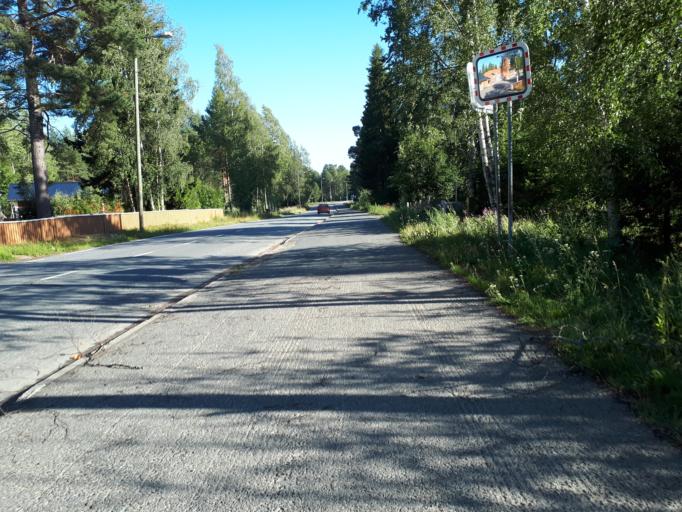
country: FI
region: Northern Ostrobothnia
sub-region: Oulunkaari
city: Ii
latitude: 65.3184
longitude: 25.3847
